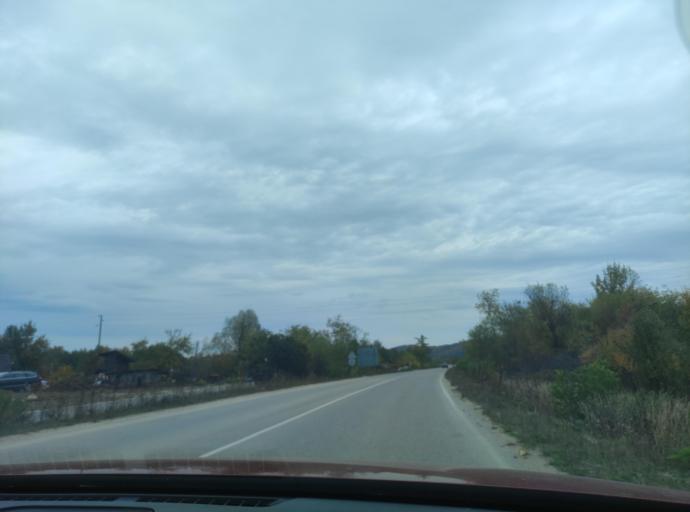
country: BG
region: Montana
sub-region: Obshtina Berkovitsa
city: Berkovitsa
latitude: 43.2450
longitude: 23.1647
